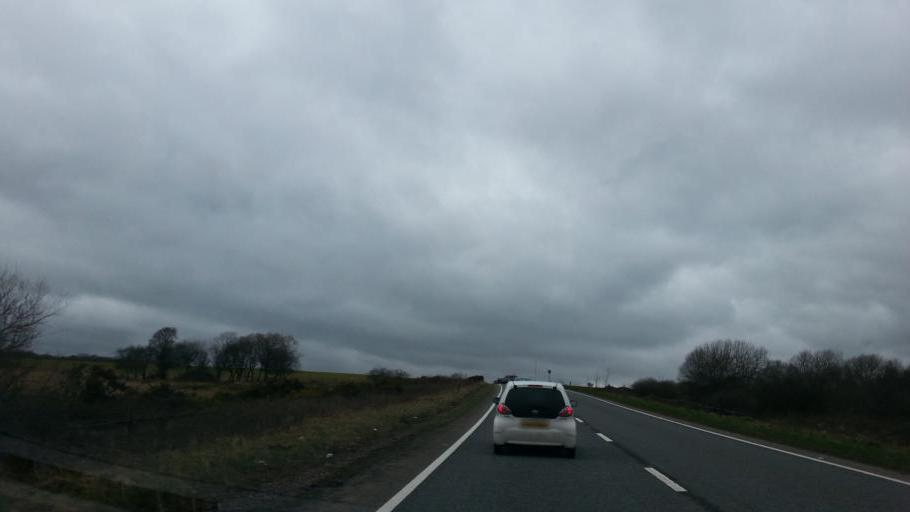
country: GB
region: England
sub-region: Devon
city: Tiverton
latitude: 50.9721
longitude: -3.6236
